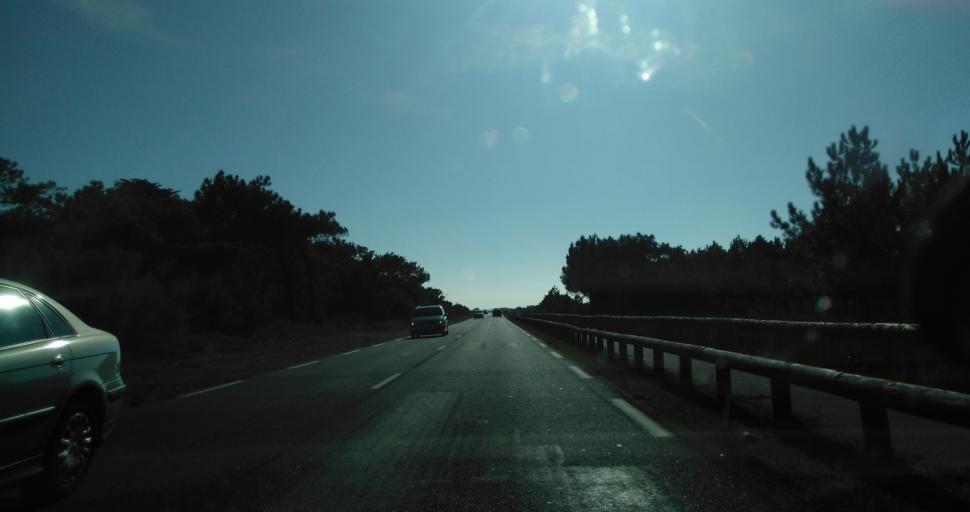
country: FR
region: Brittany
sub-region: Departement du Morbihan
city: Plouharnel
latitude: 47.5880
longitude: -3.1333
